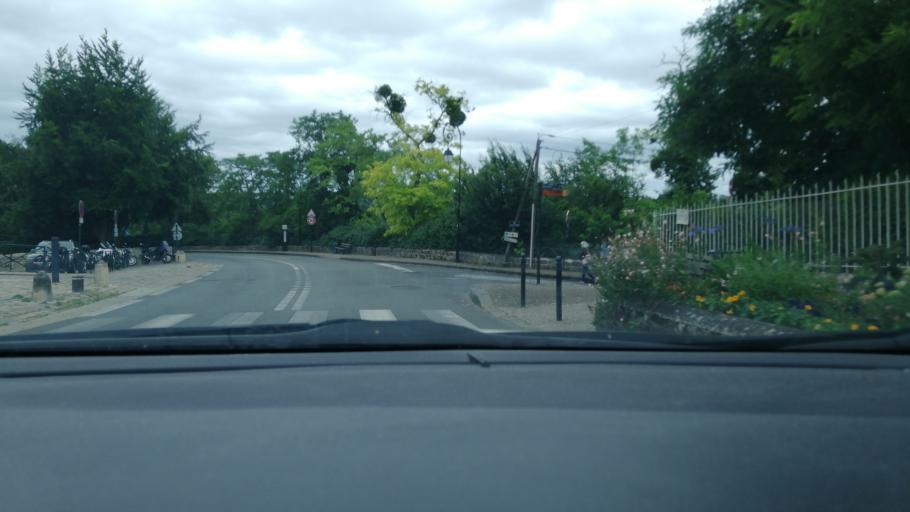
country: FR
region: Ile-de-France
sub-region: Departement du Val-d'Oise
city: Auvers-sur-Oise
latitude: 49.0716
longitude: 2.1652
